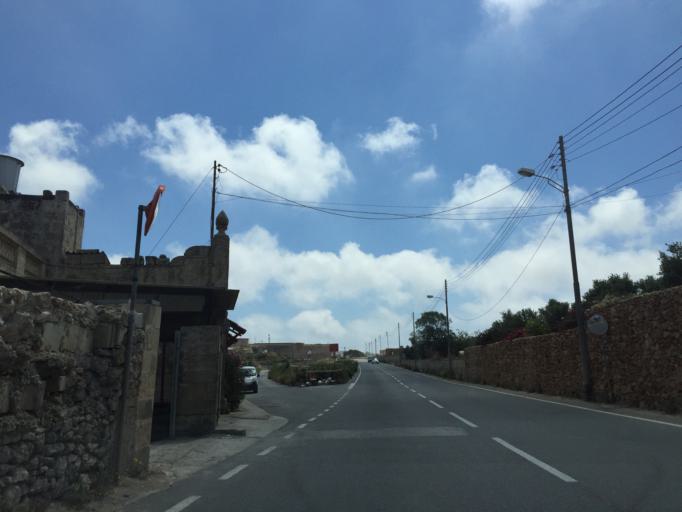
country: MT
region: Ir-Rabat
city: Rabat
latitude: 35.8727
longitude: 14.3937
